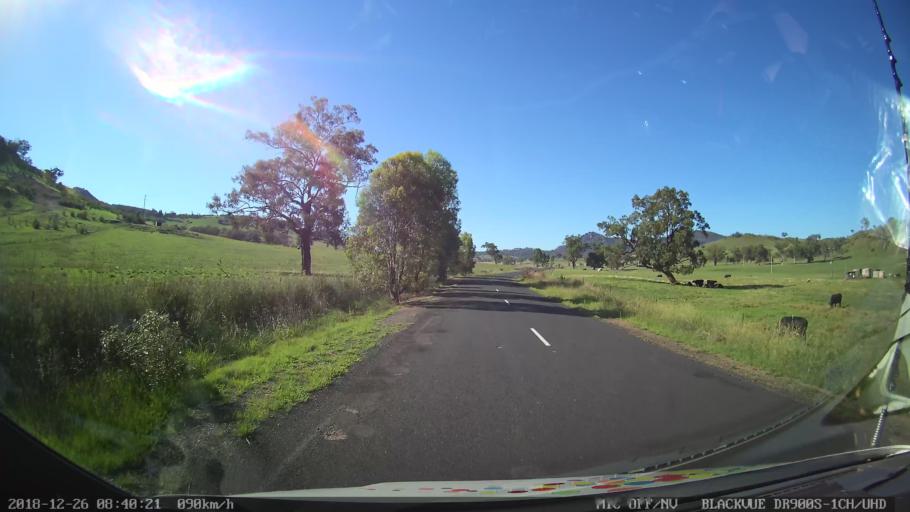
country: AU
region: New South Wales
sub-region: Mid-Western Regional
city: Kandos
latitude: -32.4657
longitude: 150.0763
